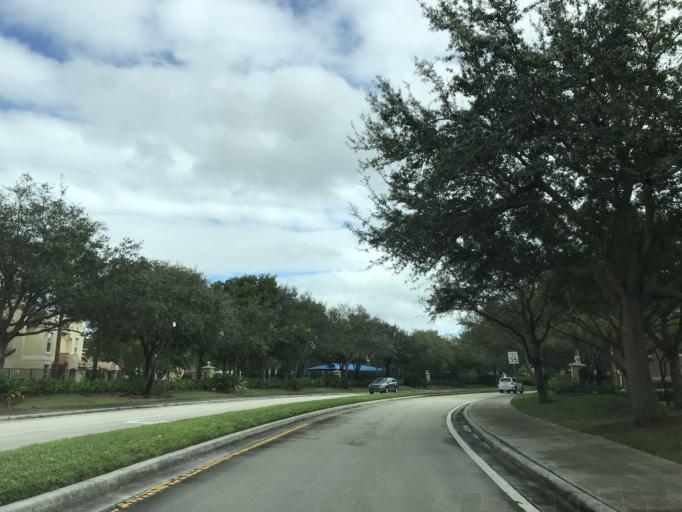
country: US
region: Florida
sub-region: Broward County
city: Coral Springs
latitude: 26.3088
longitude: -80.2768
